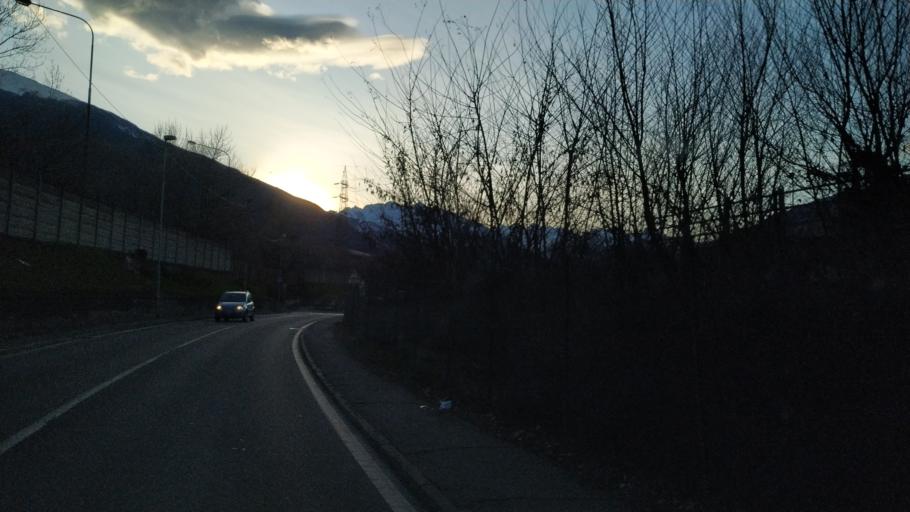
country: IT
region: Aosta Valley
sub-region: Valle d'Aosta
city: Pollein
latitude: 45.7372
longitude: 7.3358
